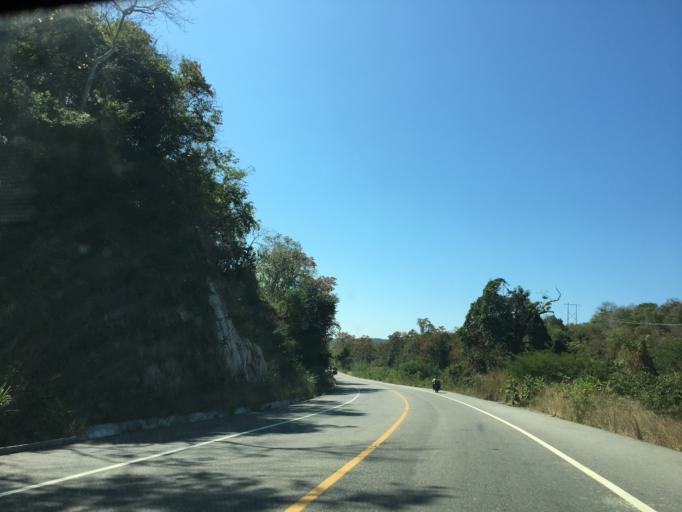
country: MX
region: Oaxaca
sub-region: Santa Maria Huatulco
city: Sector H Tres
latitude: 15.7749
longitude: -96.2253
